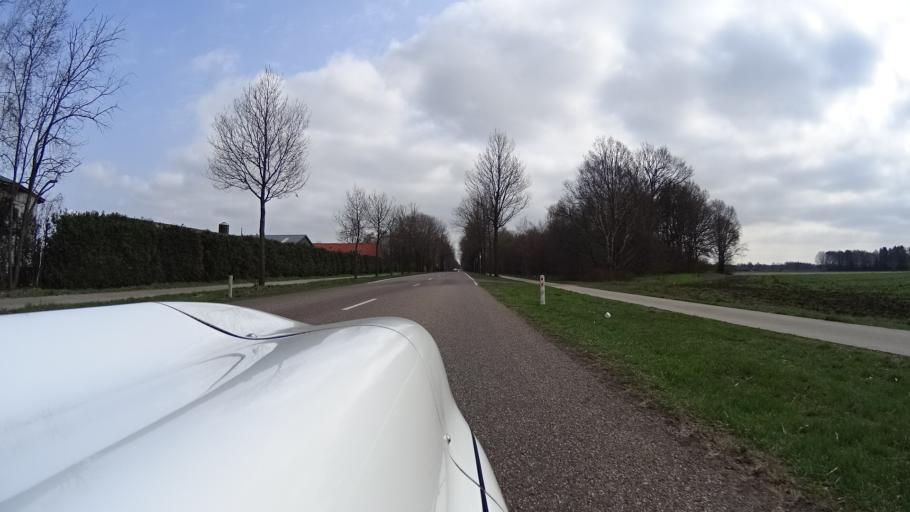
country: NL
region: North Brabant
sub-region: Gemeente Veghel
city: Zijtaart
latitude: 51.5514
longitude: 5.5376
